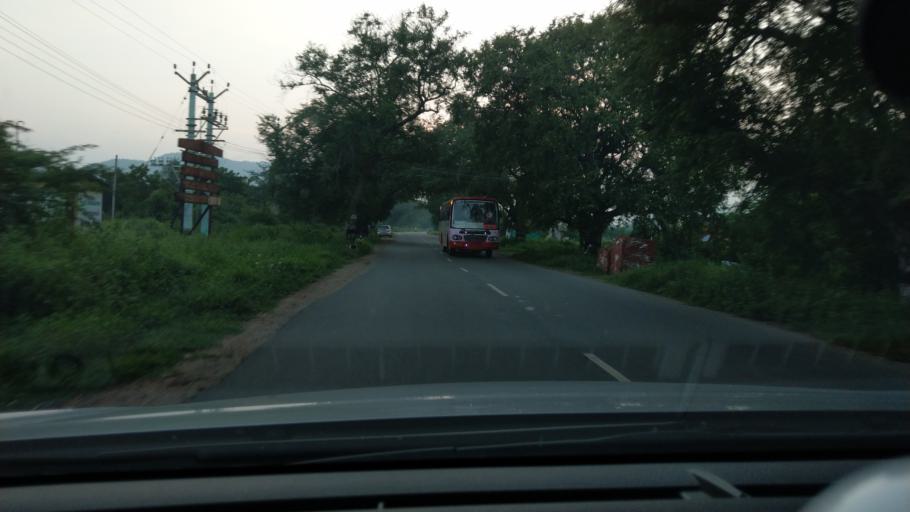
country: IN
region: Tamil Nadu
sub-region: Salem
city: Attur
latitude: 11.5970
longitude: 78.5728
